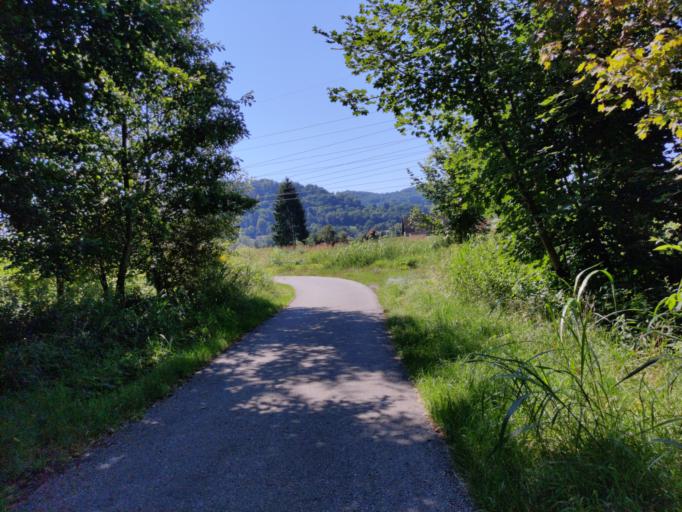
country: AT
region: Styria
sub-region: Politischer Bezirk Leibnitz
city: Wildon
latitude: 46.8943
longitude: 15.5046
